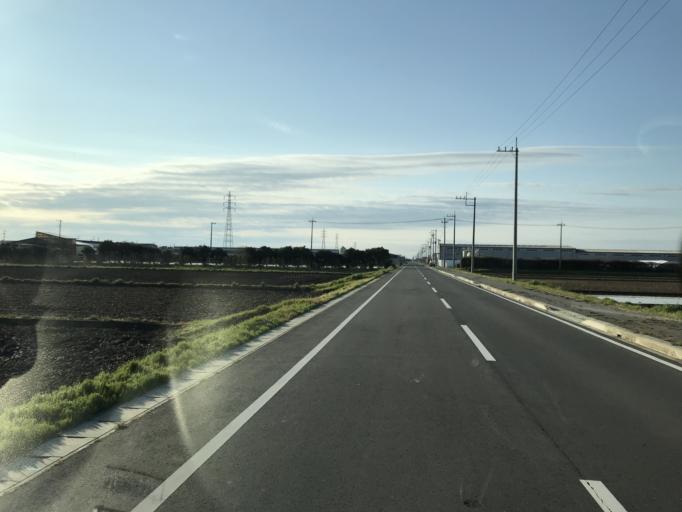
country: JP
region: Chiba
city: Yokaichiba
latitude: 35.6801
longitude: 140.5786
